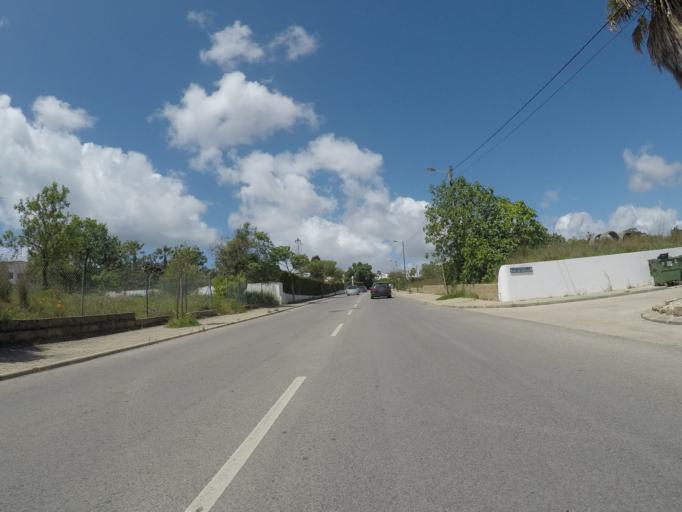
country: PT
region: Faro
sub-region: Silves
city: Armacao de Pera
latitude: 37.1038
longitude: -8.3729
